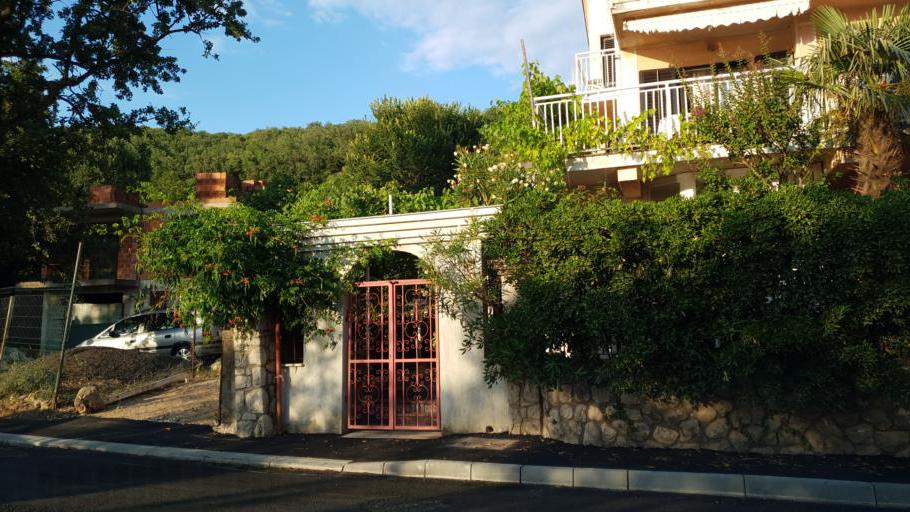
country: HR
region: Primorsko-Goranska
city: Omisalj
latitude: 45.2178
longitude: 14.5526
